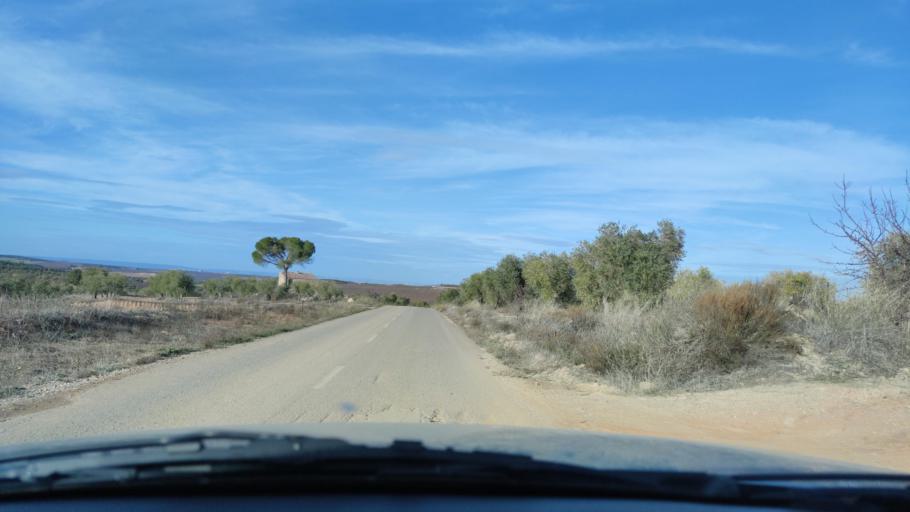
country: ES
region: Catalonia
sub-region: Provincia de Lleida
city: el Cogul
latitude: 41.4683
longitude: 0.6680
